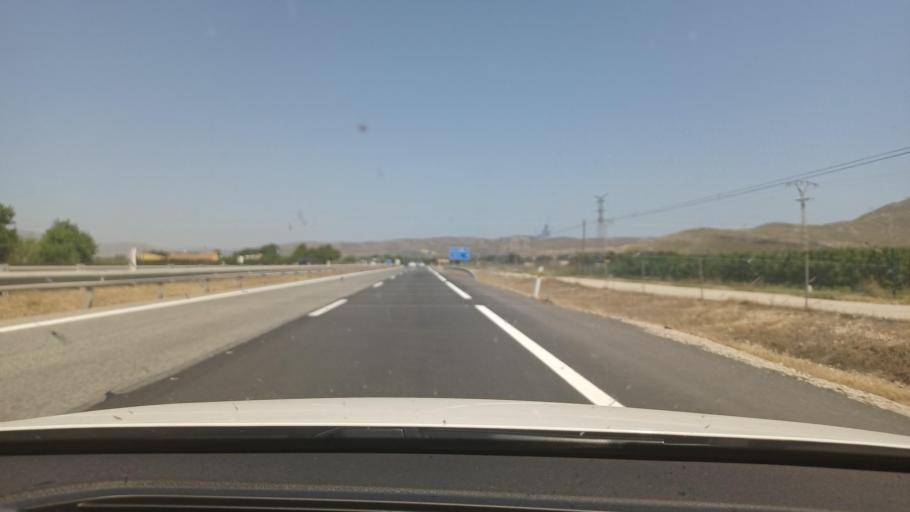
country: ES
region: Valencia
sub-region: Provincia de Alicante
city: Villena
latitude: 38.6604
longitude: -0.8783
